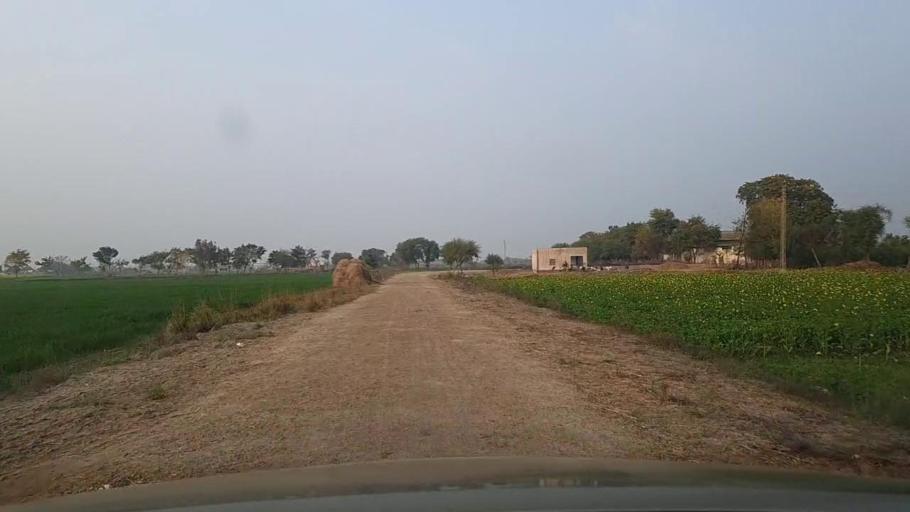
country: PK
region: Sindh
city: Sanghar
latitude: 26.1867
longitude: 68.9441
